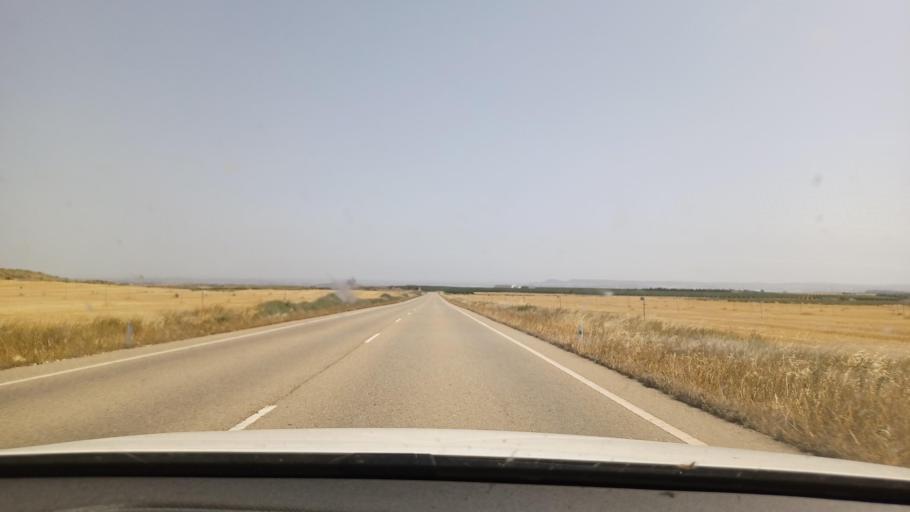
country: ES
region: Aragon
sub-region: Provincia de Zaragoza
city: Chiprana
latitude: 41.3157
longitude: -0.0766
